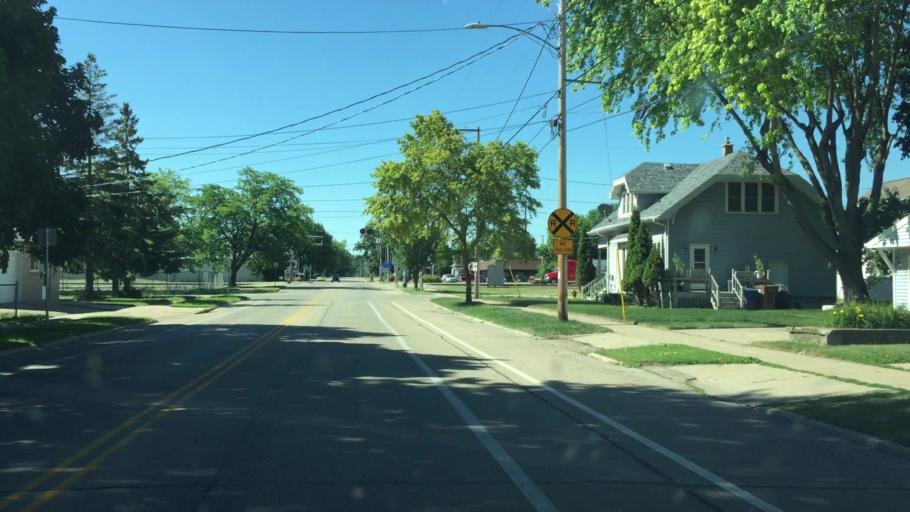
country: US
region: Wisconsin
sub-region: Winnebago County
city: Menasha
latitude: 44.2070
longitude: -88.4401
